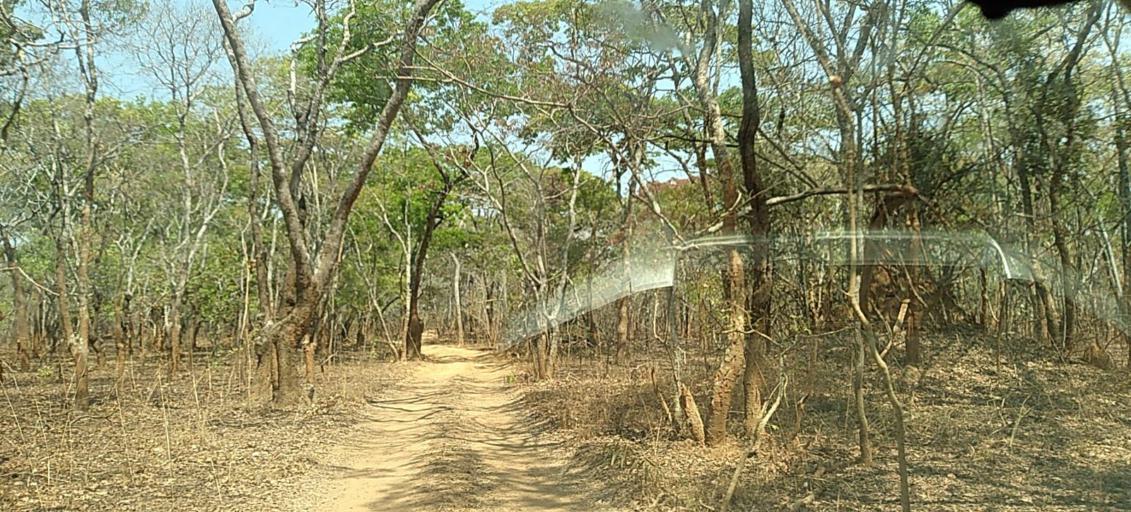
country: ZM
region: North-Western
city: Kasempa
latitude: -13.3939
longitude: 25.5901
